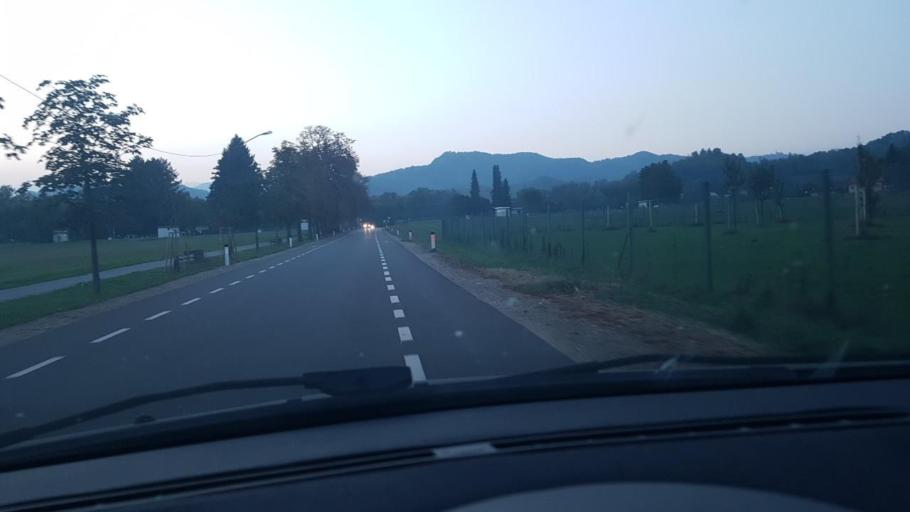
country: SI
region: Maribor
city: Kamnica
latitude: 46.5689
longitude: 15.6301
